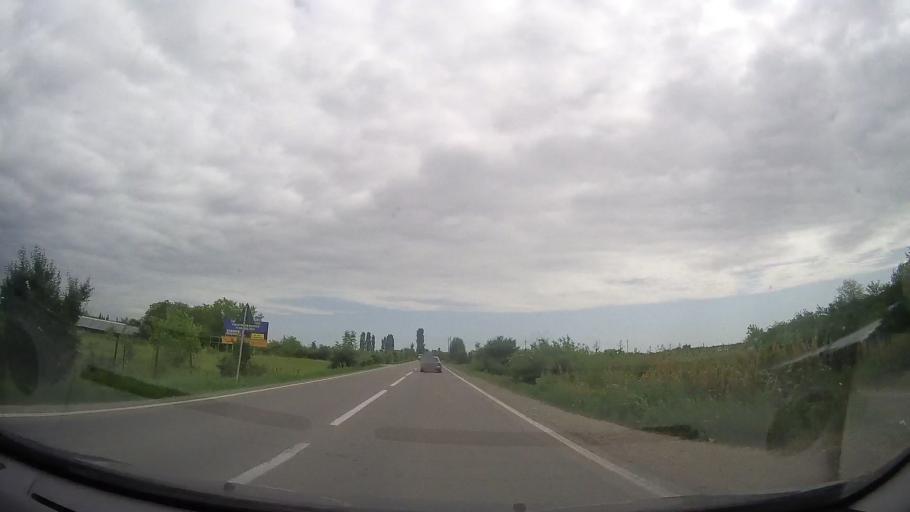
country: RO
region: Prahova
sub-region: Comuna Barcanesti
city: Barcanesti
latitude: 44.8899
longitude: 26.0477
